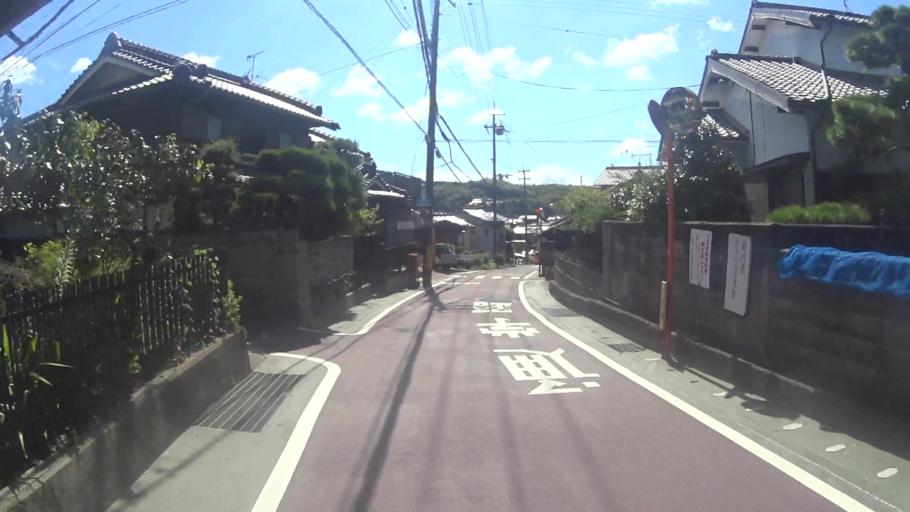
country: JP
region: Kyoto
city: Tanabe
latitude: 34.8181
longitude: 135.8076
